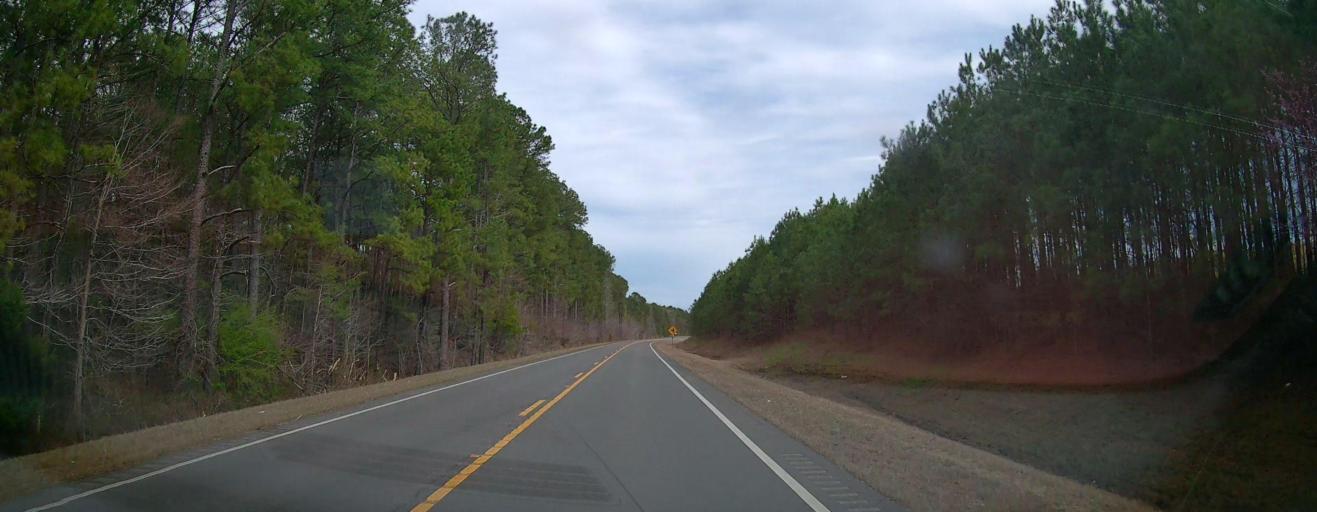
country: US
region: Alabama
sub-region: Walker County
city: Jasper
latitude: 33.8637
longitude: -87.3970
